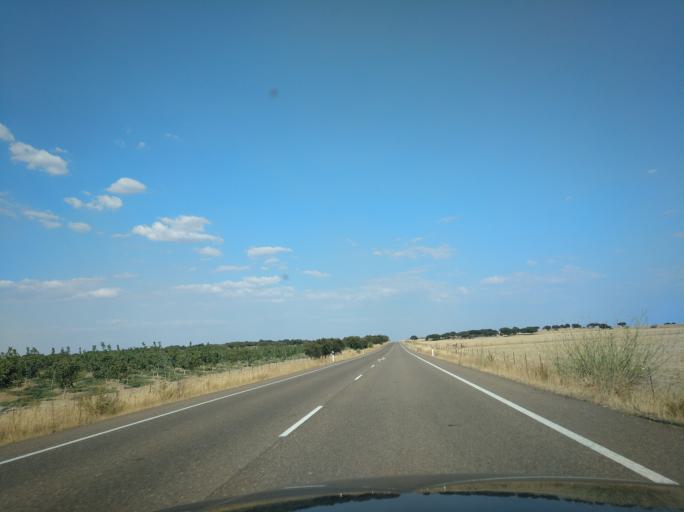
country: ES
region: Extremadura
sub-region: Provincia de Badajoz
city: Villanueva del Fresno
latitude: 38.3798
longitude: -7.2349
